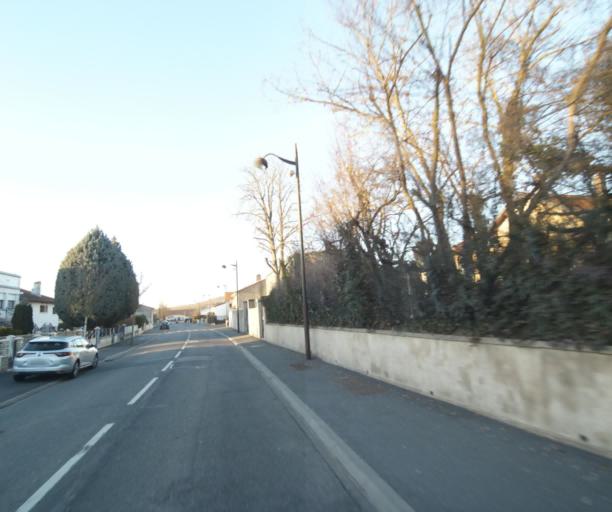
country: FR
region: Lorraine
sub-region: Departement de Meurthe-et-Moselle
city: Pulnoy
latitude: 48.7030
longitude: 6.2581
